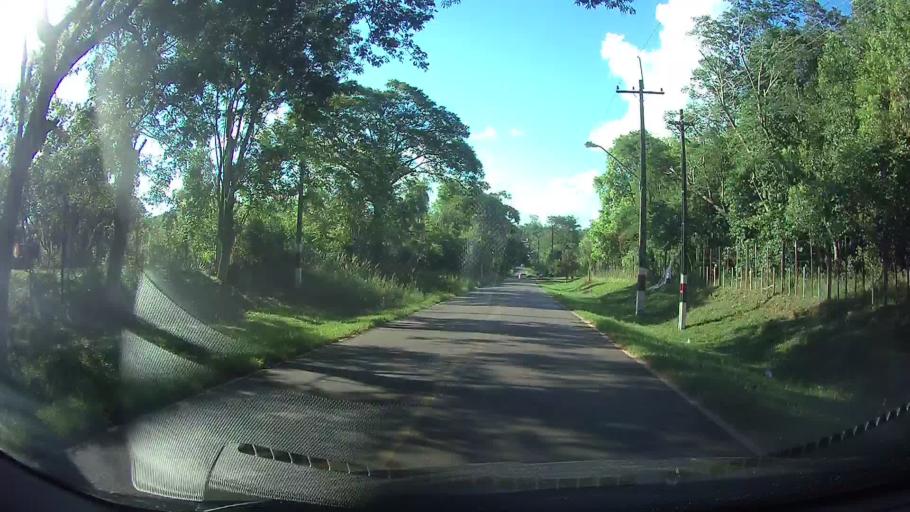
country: PY
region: Central
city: Aregua
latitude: -25.3279
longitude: -57.3867
